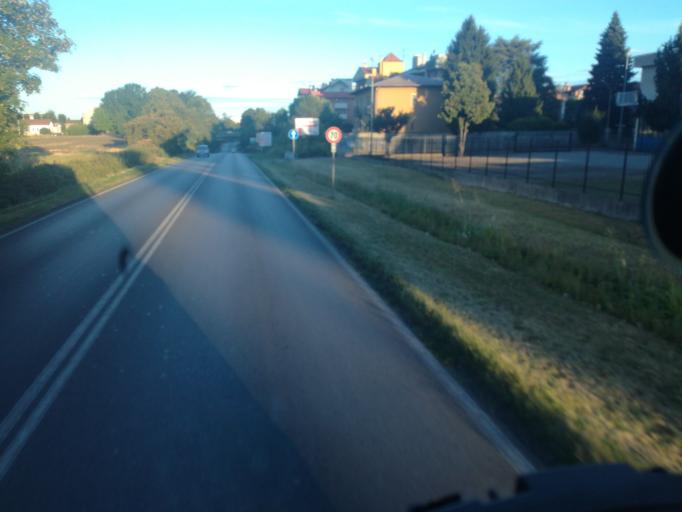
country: IT
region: Lombardy
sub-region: Provincia di Monza e Brianza
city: Bovisio-Masciago
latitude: 45.6041
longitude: 9.1507
